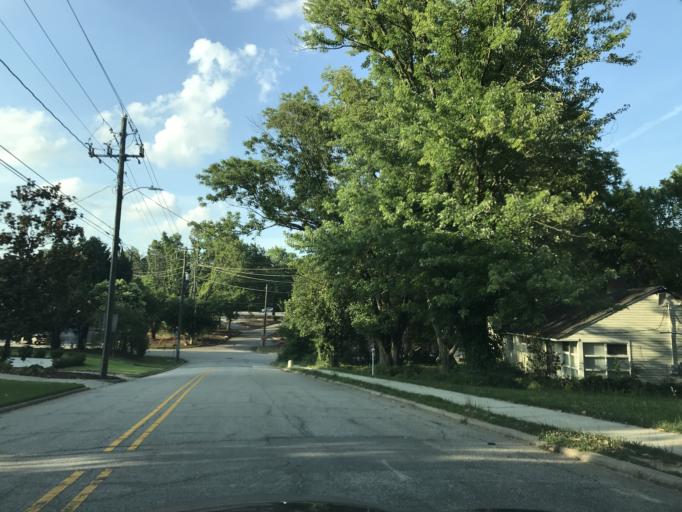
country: US
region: North Carolina
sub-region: Wake County
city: West Raleigh
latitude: 35.7956
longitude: -78.6554
